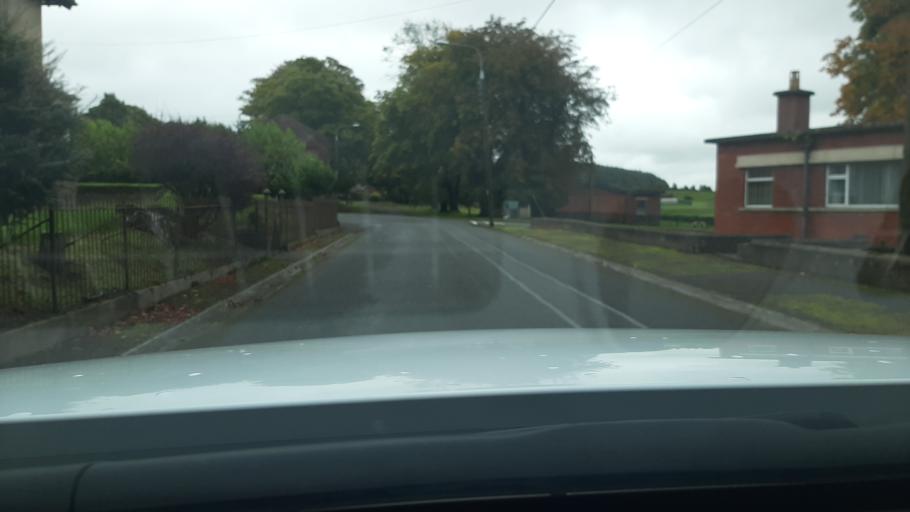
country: IE
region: Leinster
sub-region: Kildare
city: Athgarvan
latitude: 53.1449
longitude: -6.8241
